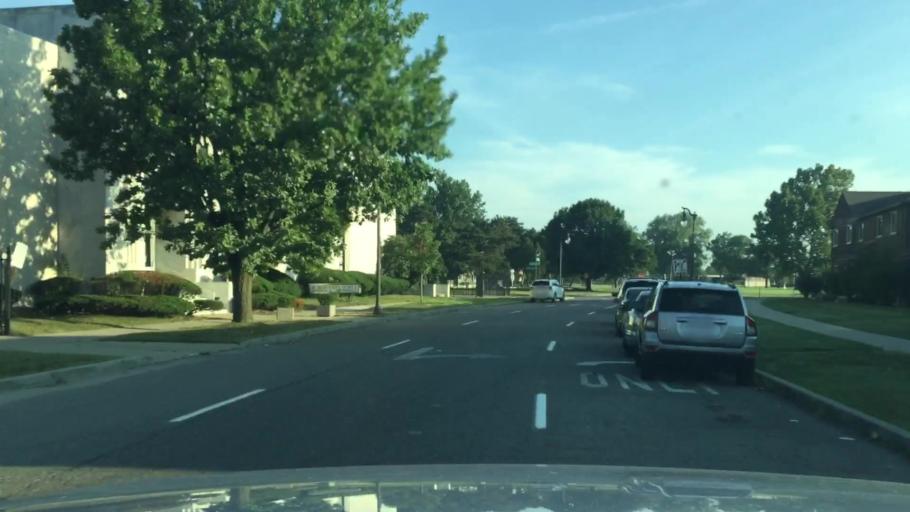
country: US
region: Michigan
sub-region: Wayne County
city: Highland Park
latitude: 42.4180
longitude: -83.1095
